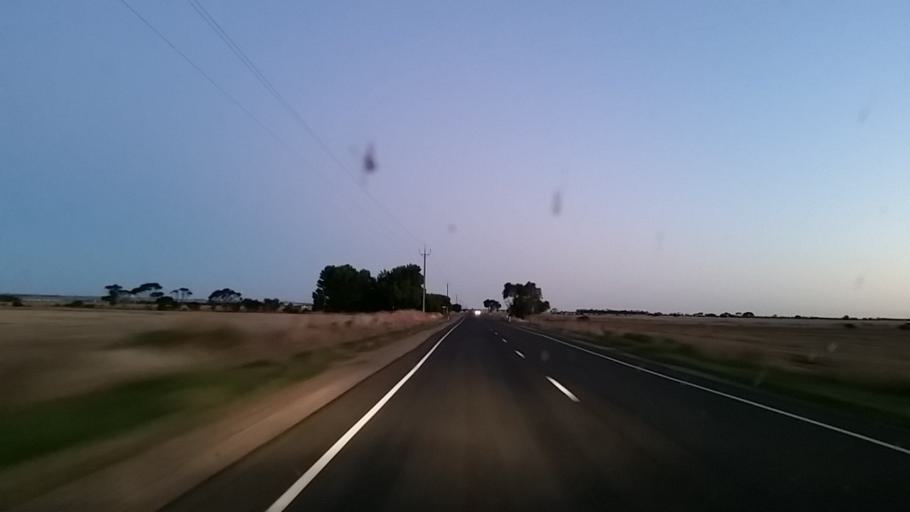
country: AU
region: South Australia
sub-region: Wakefield
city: Balaklava
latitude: -34.1812
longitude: 138.4457
